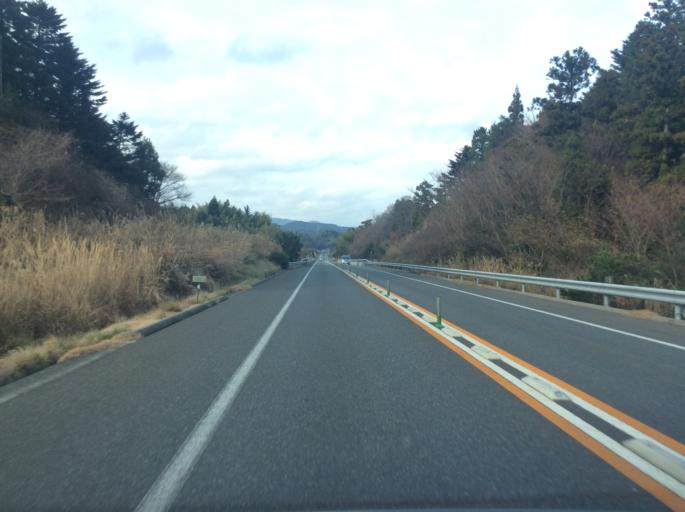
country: JP
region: Fukushima
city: Iwaki
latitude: 37.2072
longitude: 140.9831
